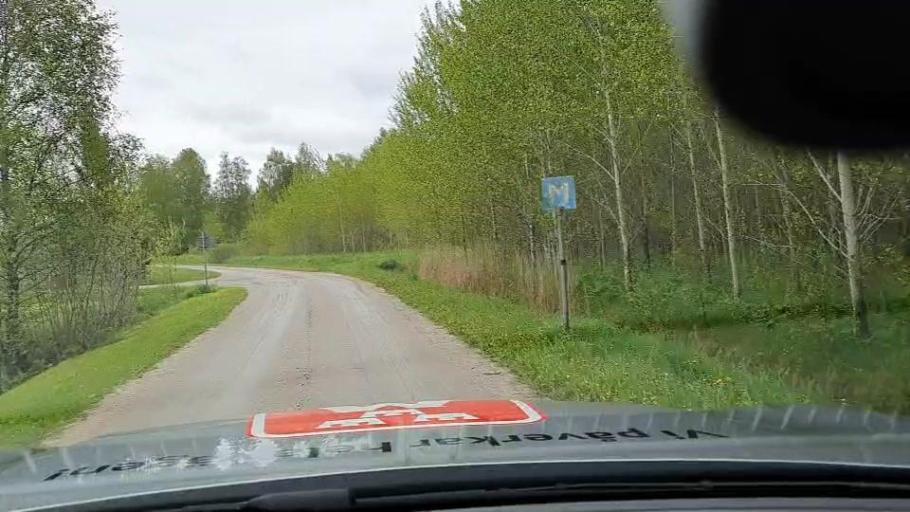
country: SE
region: Soedermanland
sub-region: Nykopings Kommun
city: Svalsta
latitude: 58.6228
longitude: 16.9379
